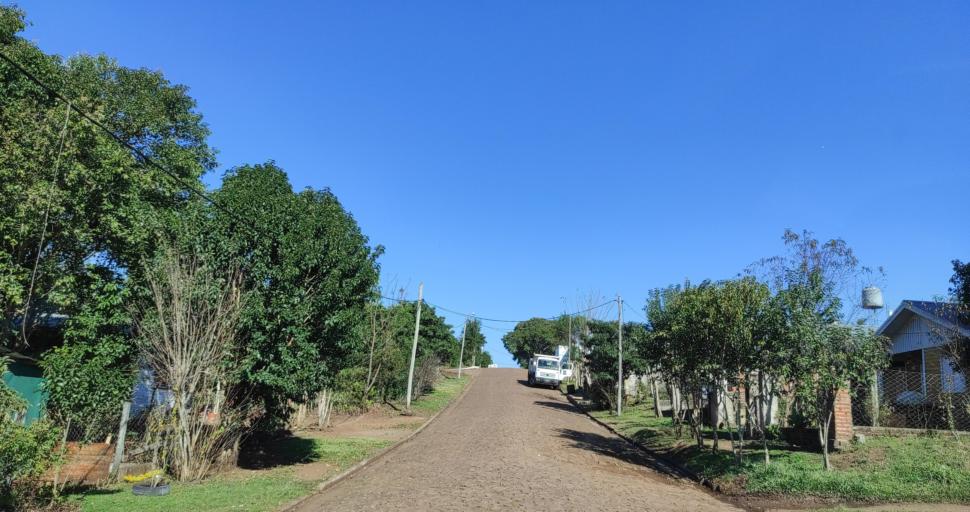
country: AR
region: Misiones
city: Cerro Cora
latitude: -27.6284
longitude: -55.7051
